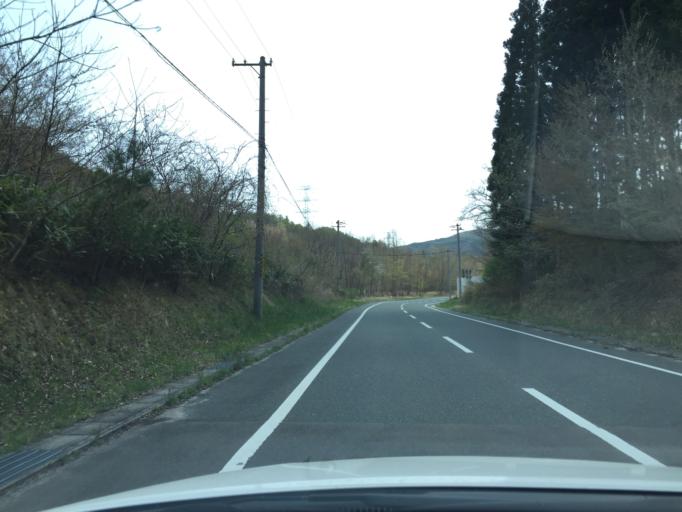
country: JP
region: Fukushima
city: Iwaki
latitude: 37.2793
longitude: 140.8389
